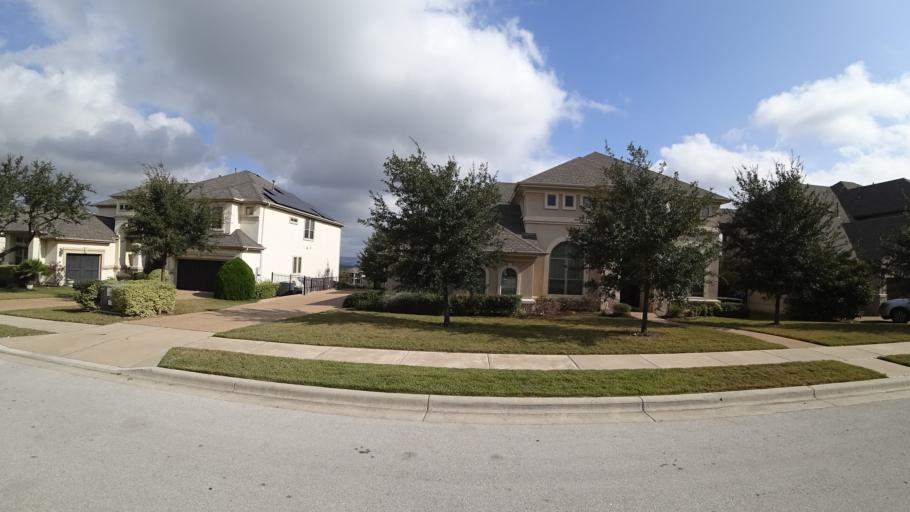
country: US
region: Texas
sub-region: Travis County
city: Barton Creek
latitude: 30.3128
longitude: -97.9018
